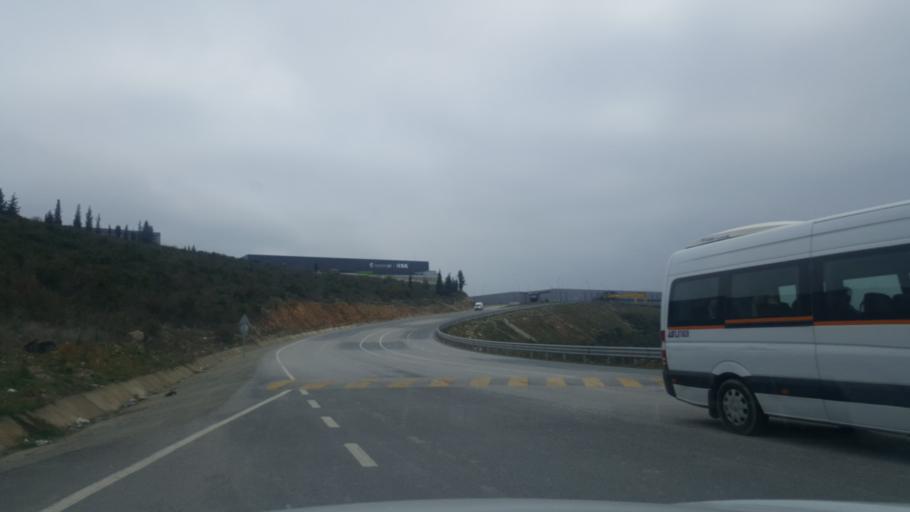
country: TR
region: Kocaeli
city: Tavsanli
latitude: 40.8401
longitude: 29.5527
